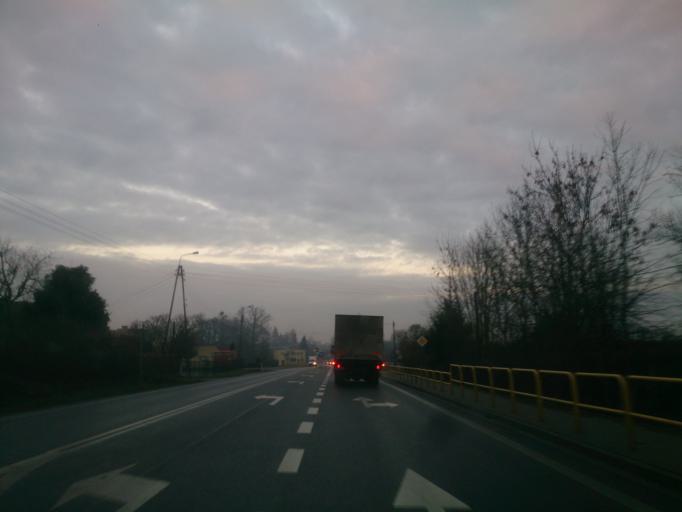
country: PL
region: Kujawsko-Pomorskie
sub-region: Powiat swiecki
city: Warlubie
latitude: 53.5836
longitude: 18.6365
